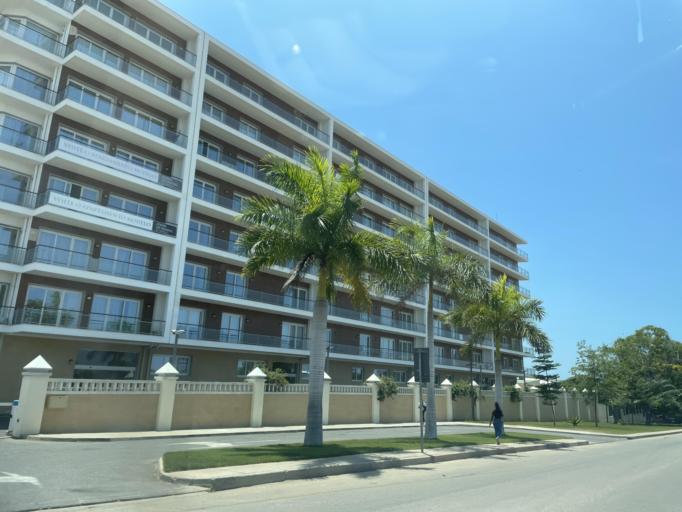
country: AO
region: Luanda
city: Luanda
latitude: -8.9072
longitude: 13.1996
